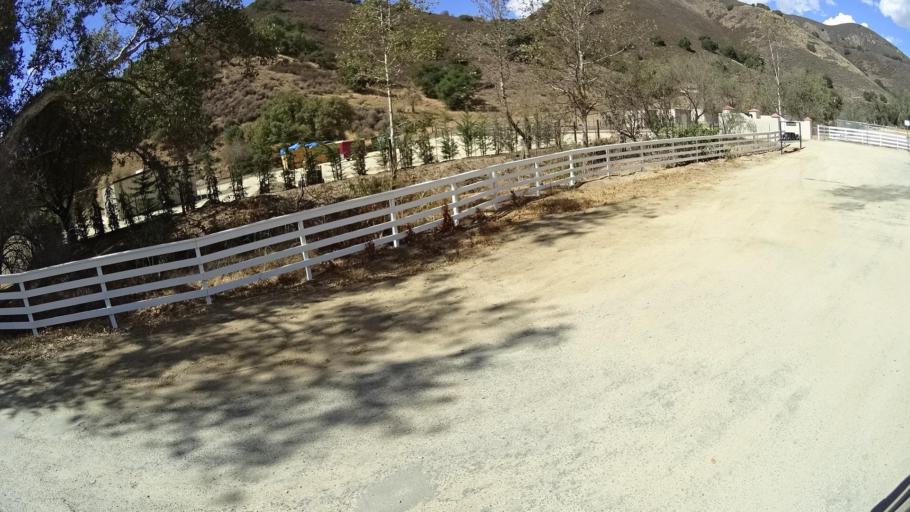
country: US
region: California
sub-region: Monterey County
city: Gonzales
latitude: 36.6051
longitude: -121.3973
